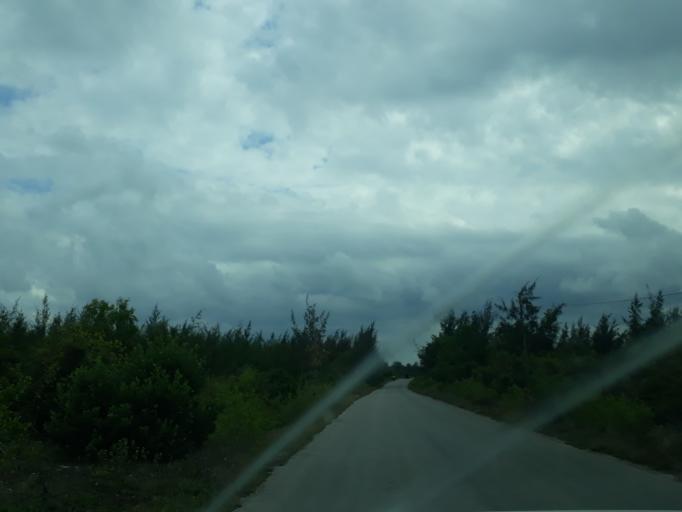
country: TZ
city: Kiwengwa
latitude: -6.0820
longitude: 39.4257
